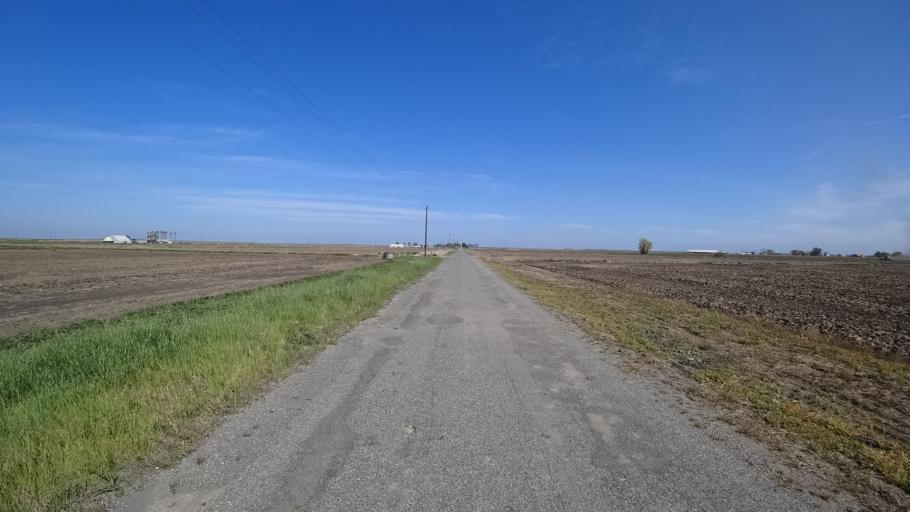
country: US
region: California
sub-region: Glenn County
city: Hamilton City
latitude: 39.6118
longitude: -122.0744
